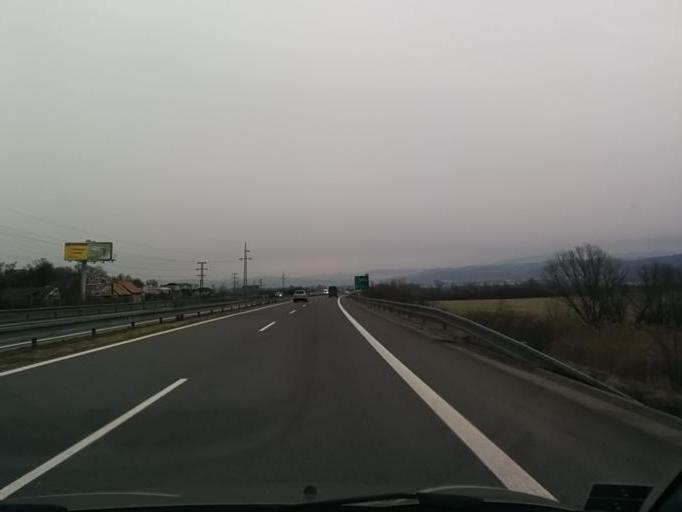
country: SK
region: Banskobystricky
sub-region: Okres Banska Bystrica
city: Zvolen
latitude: 48.5937
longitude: 19.0997
